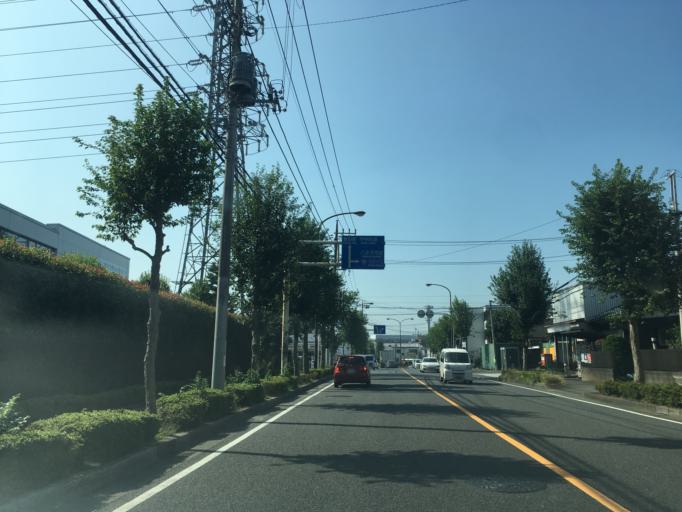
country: JP
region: Tokyo
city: Hachioji
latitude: 35.6674
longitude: 139.3585
